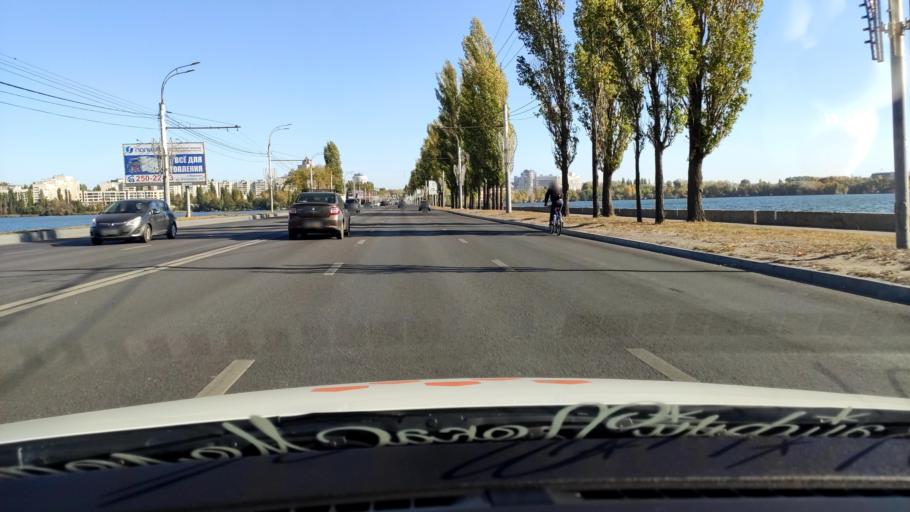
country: RU
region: Voronezj
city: Voronezh
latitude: 51.6672
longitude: 39.2306
